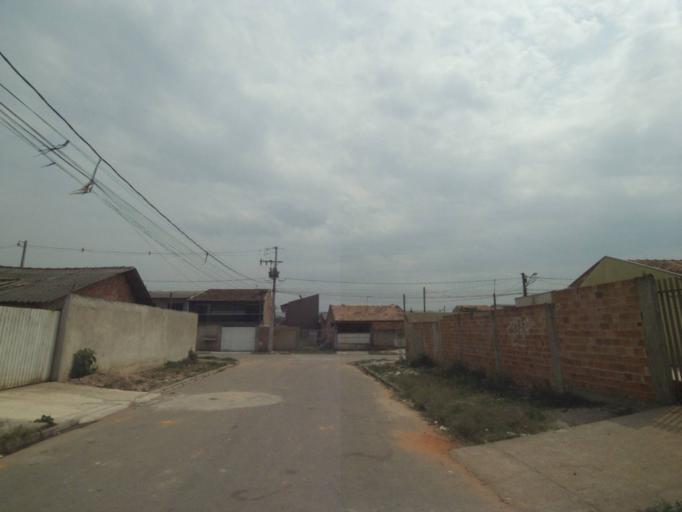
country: BR
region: Parana
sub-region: Sao Jose Dos Pinhais
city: Sao Jose dos Pinhais
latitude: -25.4953
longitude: -49.2002
